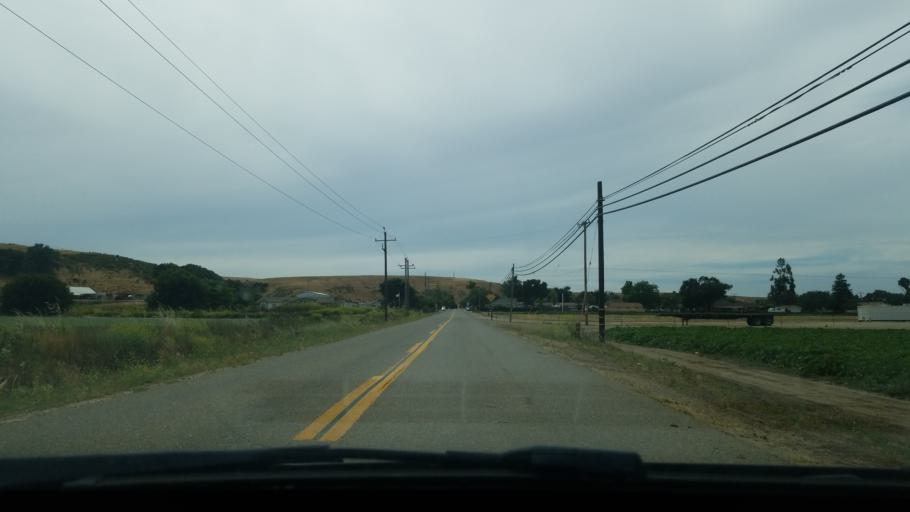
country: US
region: California
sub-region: Santa Barbara County
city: Los Alamos
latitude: 34.8645
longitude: -120.2874
